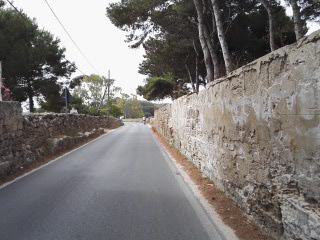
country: IT
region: Sicily
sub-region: Trapani
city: Favignana
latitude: 37.9251
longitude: 12.3359
